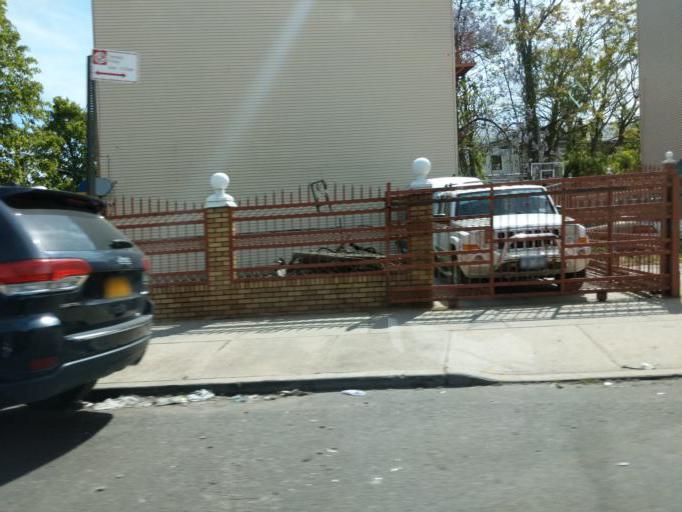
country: US
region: New York
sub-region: Kings County
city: Brooklyn
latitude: 40.6657
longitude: -73.9193
